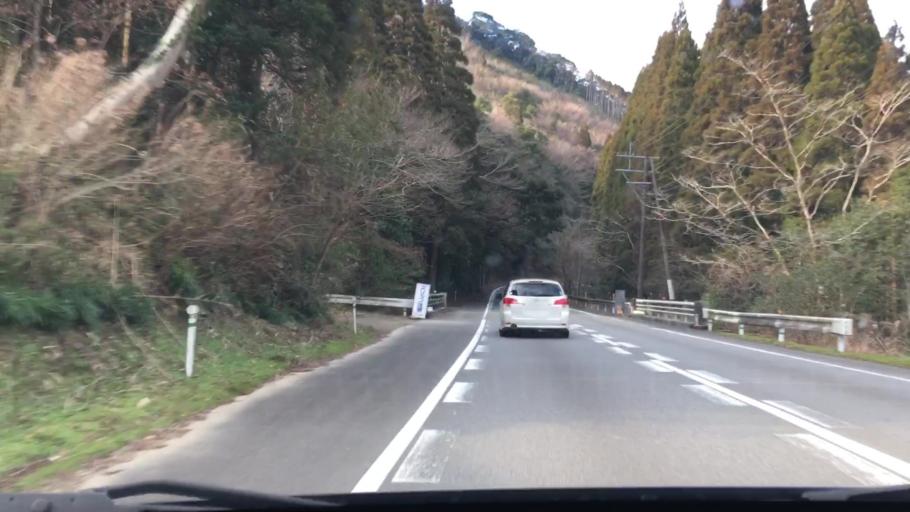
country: JP
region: Miyazaki
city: Nichinan
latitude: 31.7467
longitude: 131.3351
